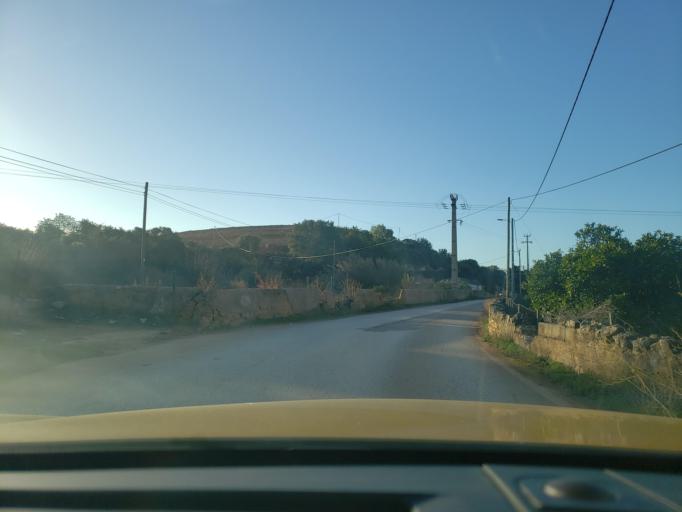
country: PT
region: Faro
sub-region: Portimao
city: Alvor
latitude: 37.1733
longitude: -8.5788
